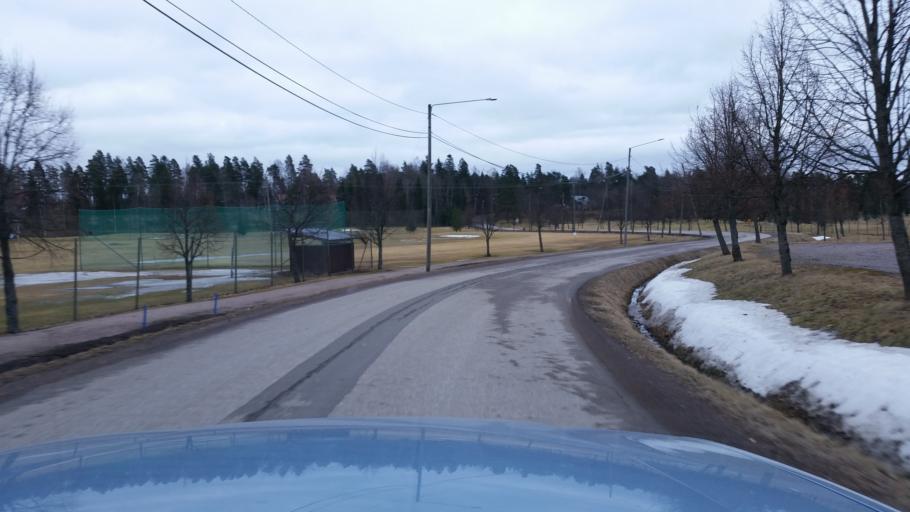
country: FI
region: Uusimaa
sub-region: Helsinki
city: Kauniainen
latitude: 60.2606
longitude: 24.6942
